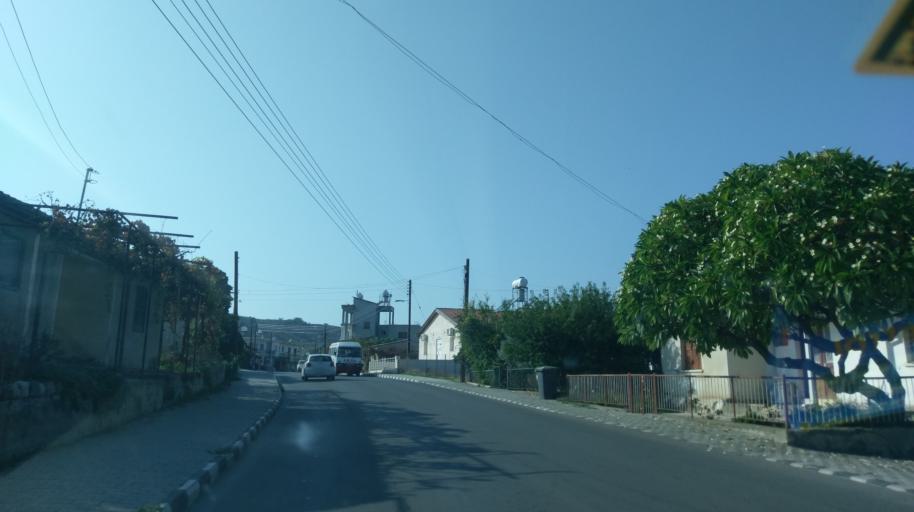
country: CY
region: Lefkosia
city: Lefka
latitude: 35.1428
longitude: 32.8110
